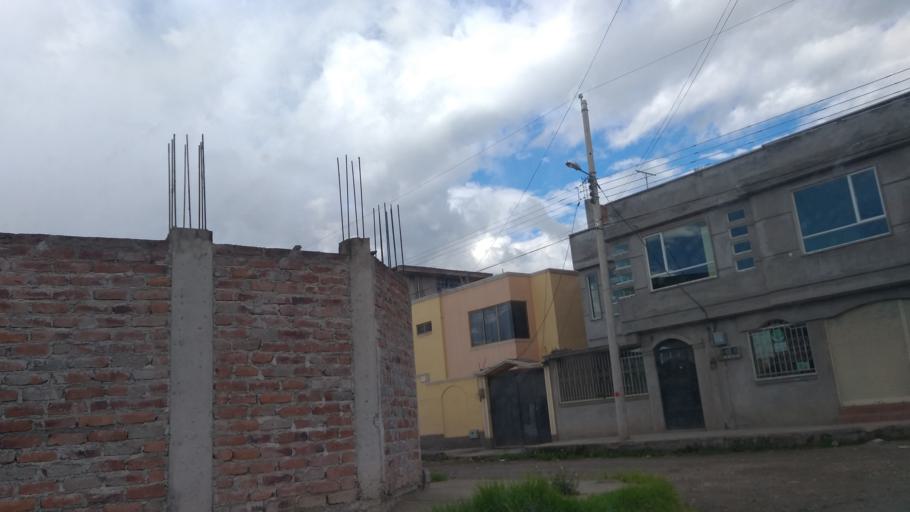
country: EC
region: Chimborazo
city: Riobamba
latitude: -1.6924
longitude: -78.6324
